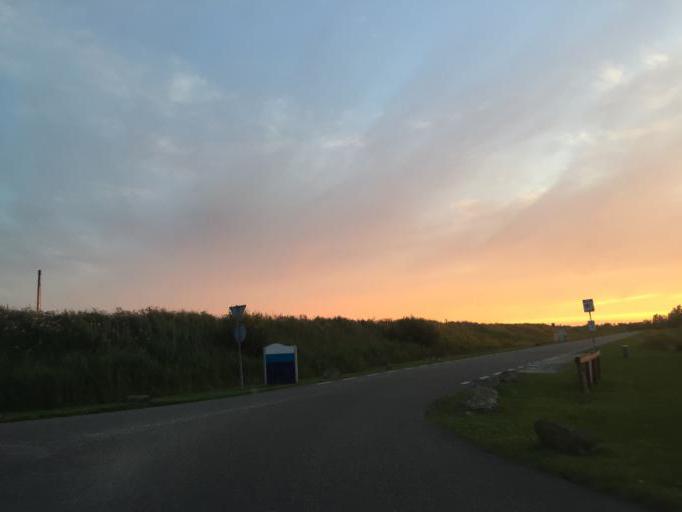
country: NL
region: Friesland
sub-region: Gemeente Dongeradeel
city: Anjum
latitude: 53.3750
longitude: 6.1589
